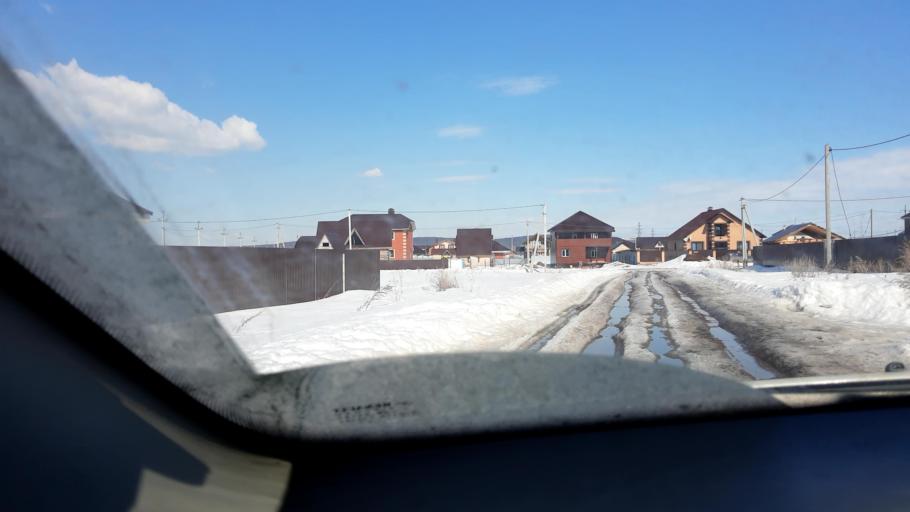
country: RU
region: Bashkortostan
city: Kabakovo
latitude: 54.5675
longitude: 56.0360
